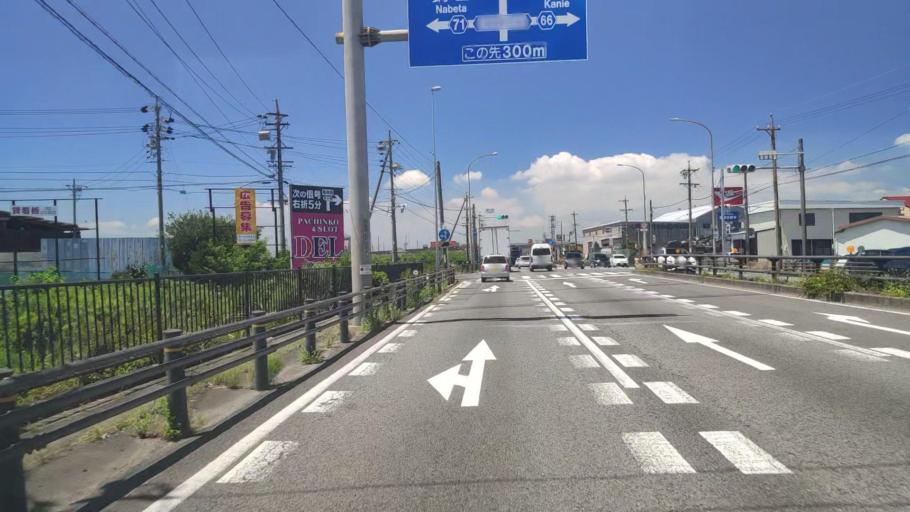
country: JP
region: Aichi
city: Kanie
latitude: 35.0768
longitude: 136.7776
